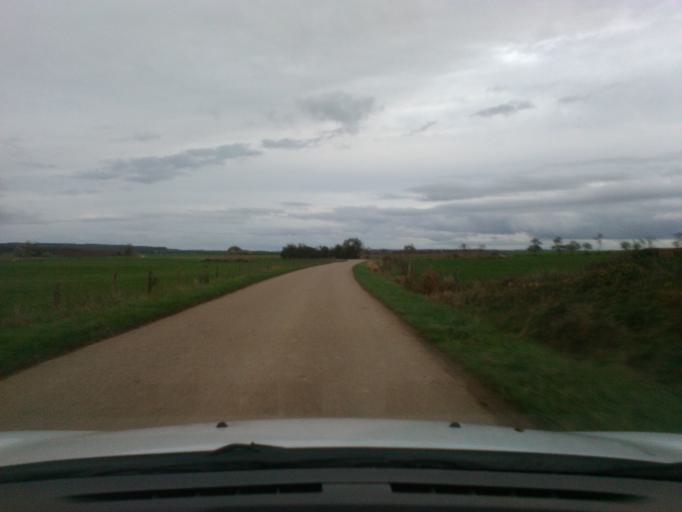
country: FR
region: Lorraine
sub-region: Departement des Vosges
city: Mirecourt
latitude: 48.3313
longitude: 6.0635
